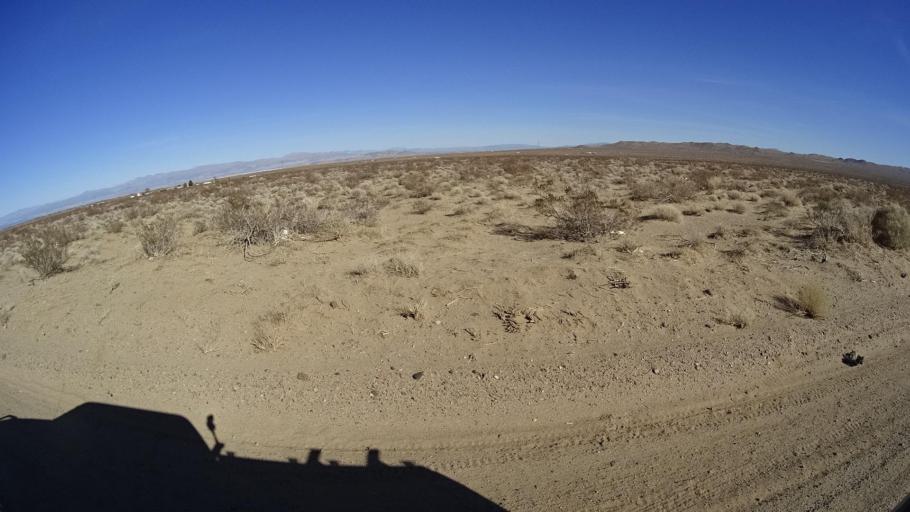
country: US
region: California
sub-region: Kern County
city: China Lake Acres
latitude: 35.5674
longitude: -117.7790
